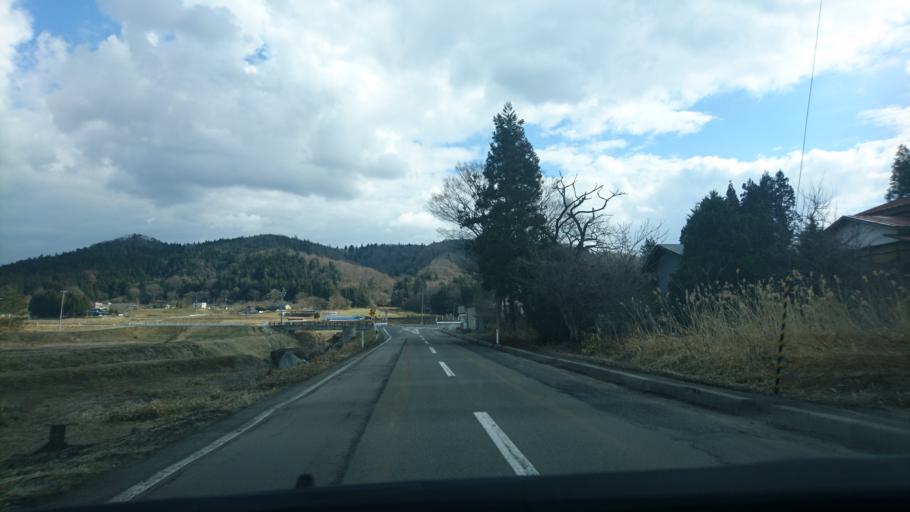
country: JP
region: Iwate
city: Hanamaki
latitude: 39.3366
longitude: 141.2387
